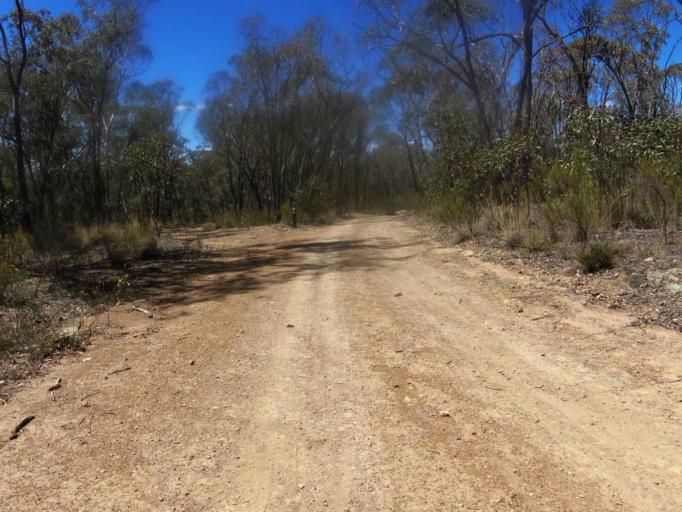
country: AU
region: Victoria
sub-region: Mount Alexander
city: Castlemaine
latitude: -37.0066
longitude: 144.1190
